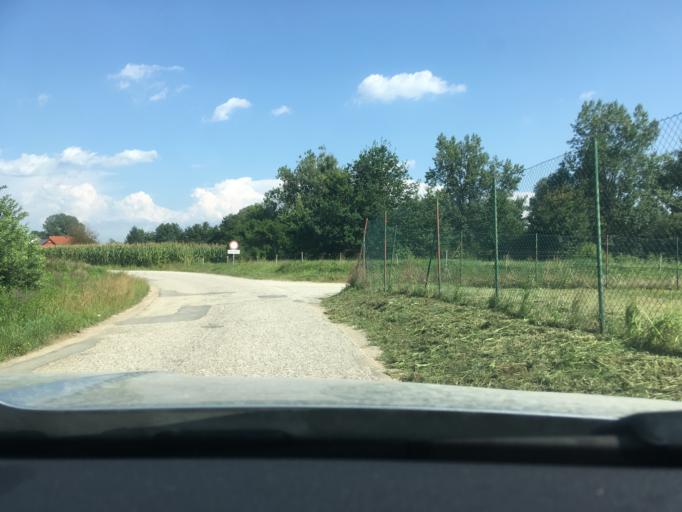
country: SI
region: Metlika
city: Metlika
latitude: 45.6469
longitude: 15.3425
